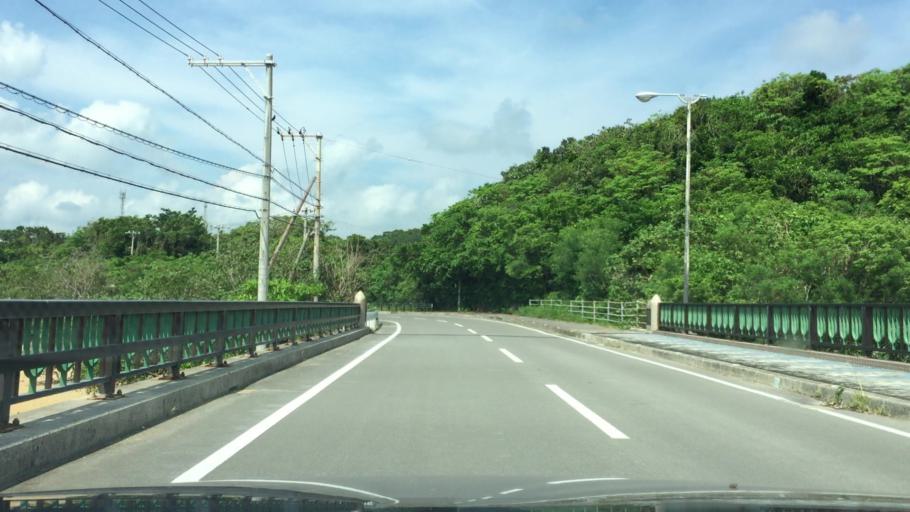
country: JP
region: Okinawa
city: Ishigaki
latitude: 24.4870
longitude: 124.2306
